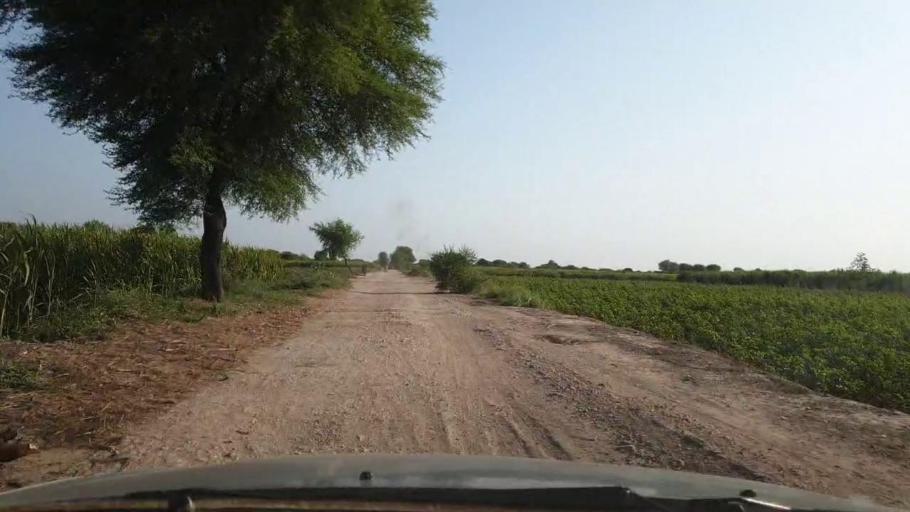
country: PK
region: Sindh
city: Tando Ghulam Ali
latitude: 25.1338
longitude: 68.9408
